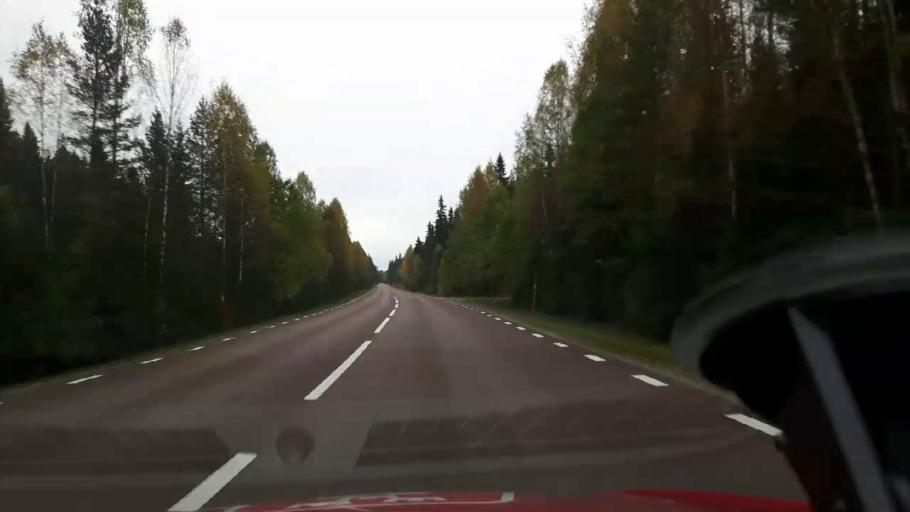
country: SE
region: Jaemtland
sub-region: Harjedalens Kommun
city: Sveg
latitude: 62.3358
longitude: 14.7301
